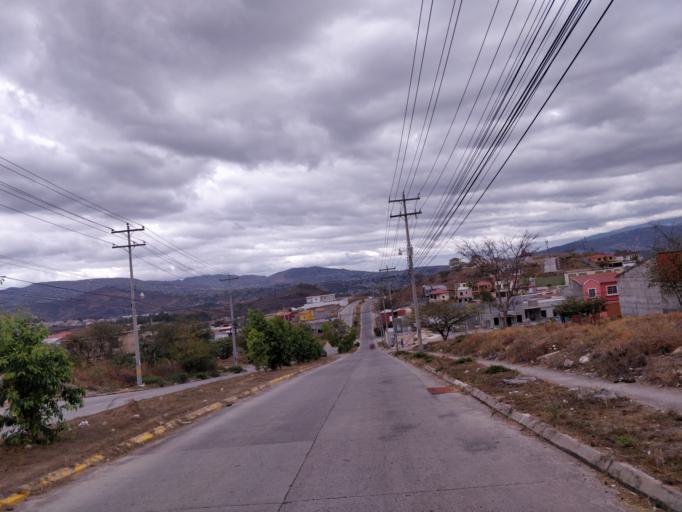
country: HN
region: Francisco Morazan
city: Yaguacire
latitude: 14.0368
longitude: -87.2375
